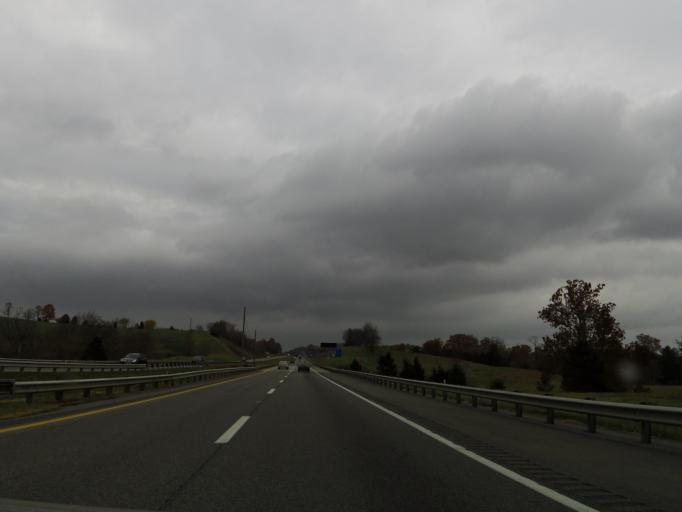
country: US
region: Virginia
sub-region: Bland County
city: Bland
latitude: 37.0736
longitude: -81.1264
